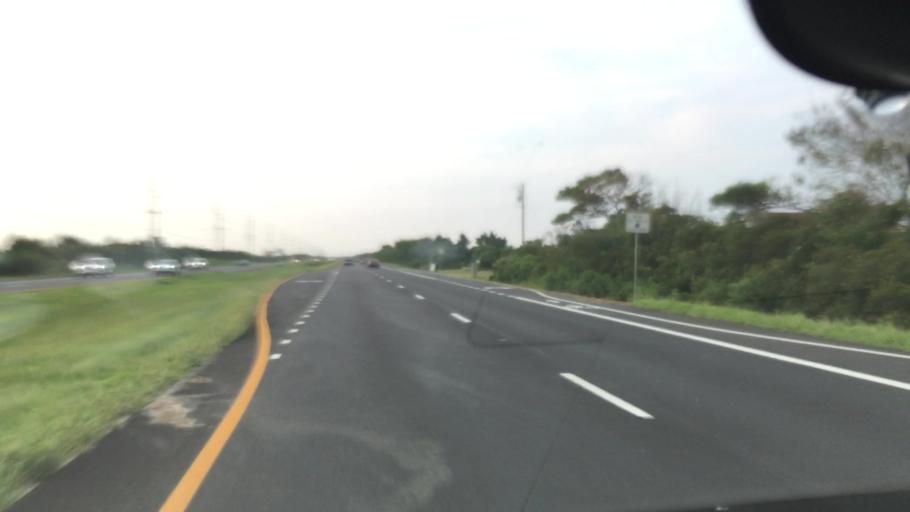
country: US
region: Delaware
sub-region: Sussex County
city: Long Neck
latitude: 38.6327
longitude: -75.0677
